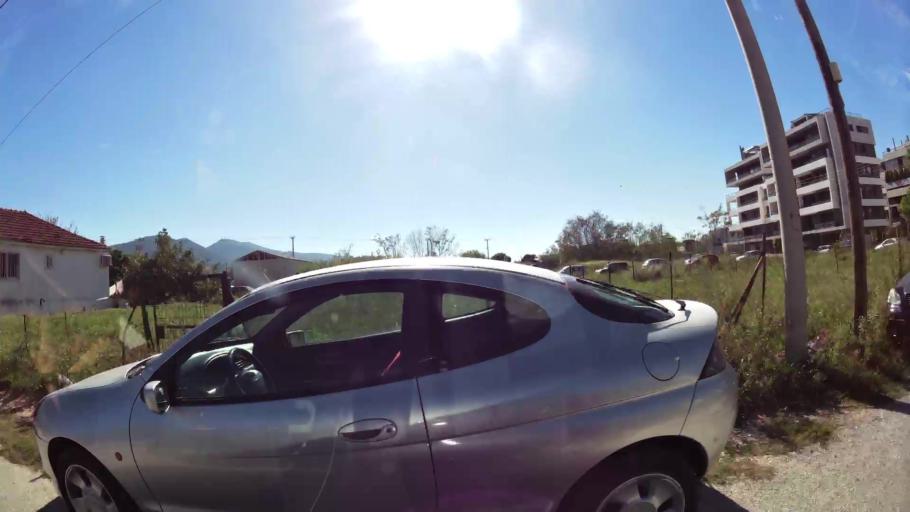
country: GR
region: Attica
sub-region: Nomarchia Athinas
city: Agia Paraskevi
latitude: 38.0223
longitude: 23.8188
